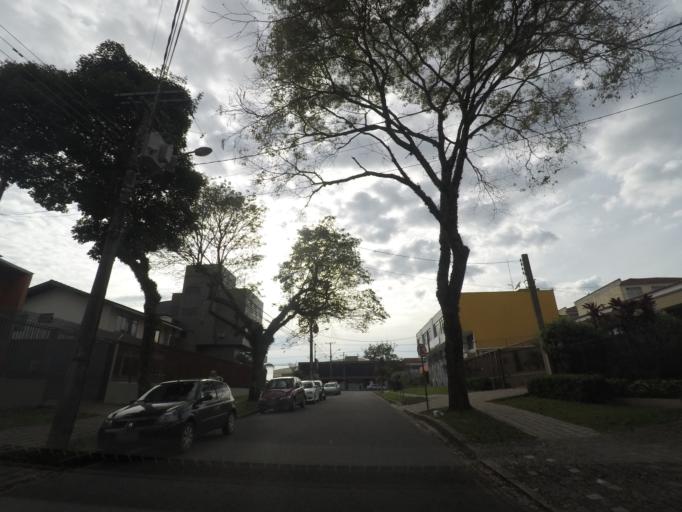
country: BR
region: Parana
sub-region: Curitiba
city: Curitiba
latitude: -25.4214
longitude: -49.2932
